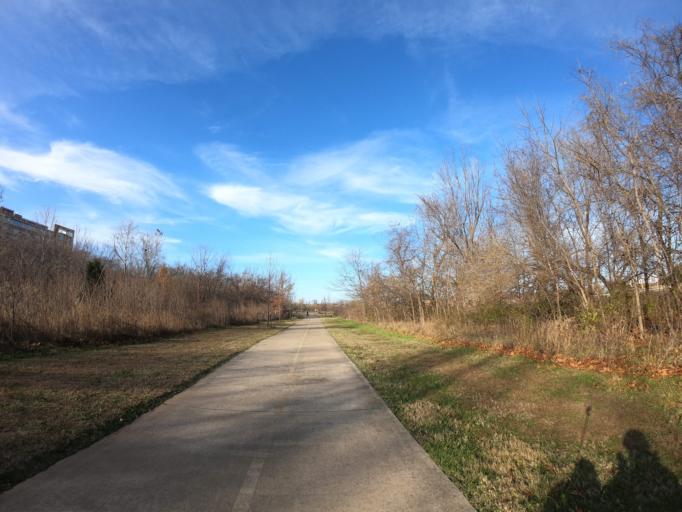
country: US
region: Arkansas
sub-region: Benton County
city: Rogers
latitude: 36.3080
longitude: -94.1807
